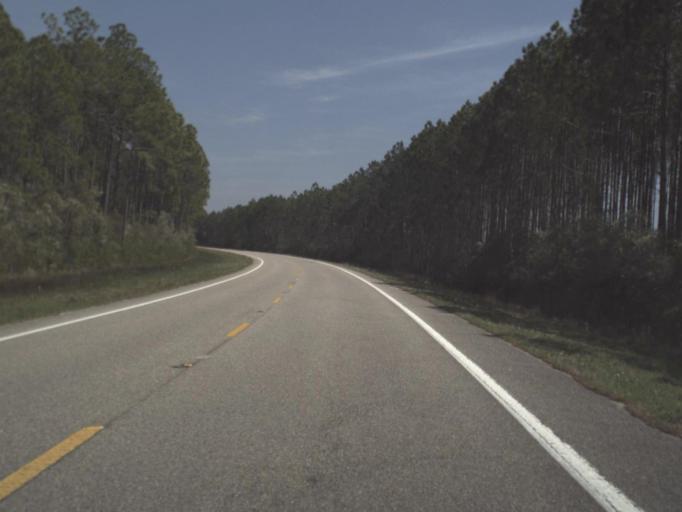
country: US
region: Florida
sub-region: Gulf County
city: Port Saint Joe
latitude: 29.7414
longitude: -85.2262
